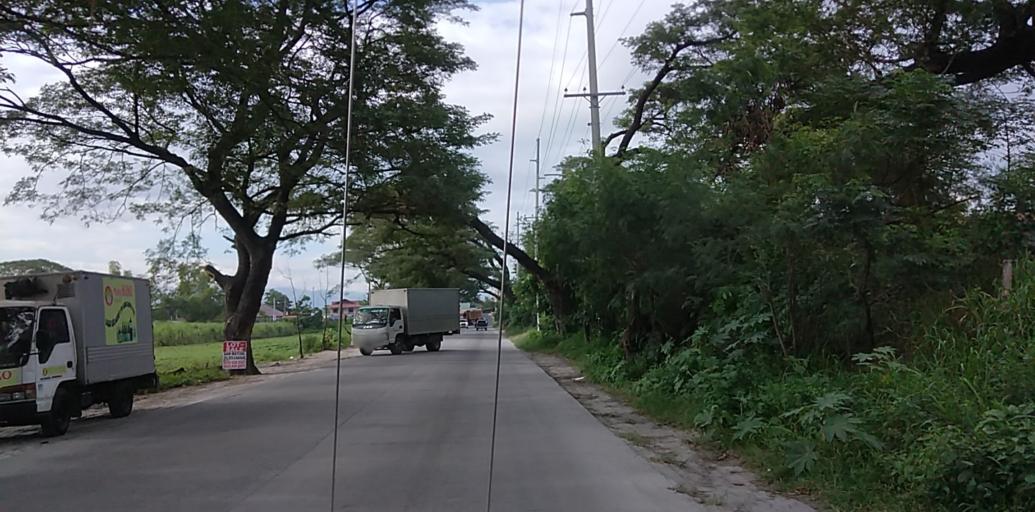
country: PH
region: Central Luzon
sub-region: Province of Pampanga
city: Porac
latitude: 15.0783
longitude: 120.5487
